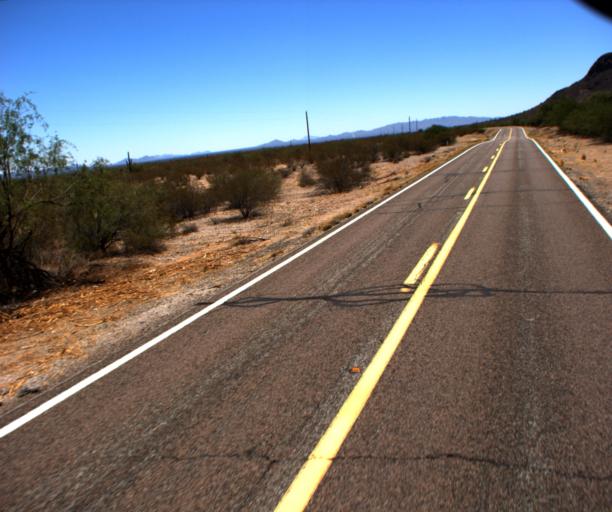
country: US
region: Arizona
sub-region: Pima County
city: Ajo
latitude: 32.2043
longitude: -112.5454
